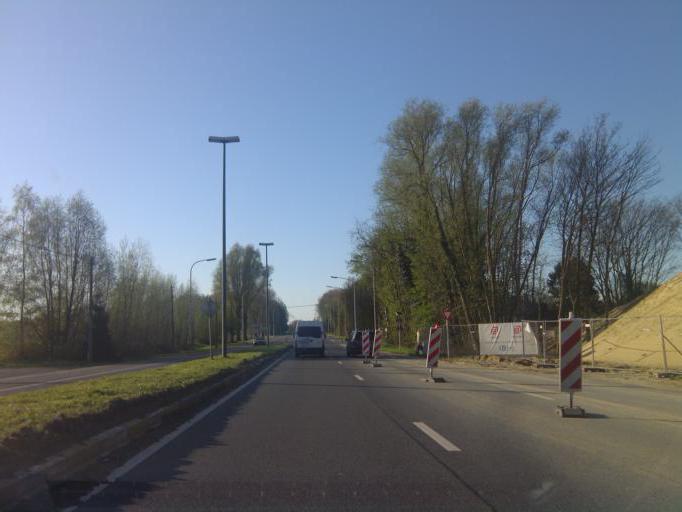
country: BE
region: Wallonia
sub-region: Province du Brabant Wallon
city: Louvain-la-Neuve
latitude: 50.6746
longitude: 4.6237
